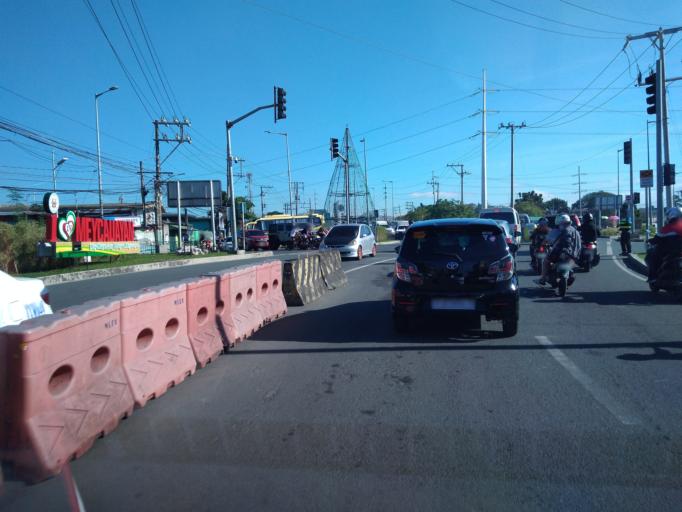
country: PH
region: Central Luzon
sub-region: Province of Bulacan
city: Meycauayan
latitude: 14.7447
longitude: 120.9716
